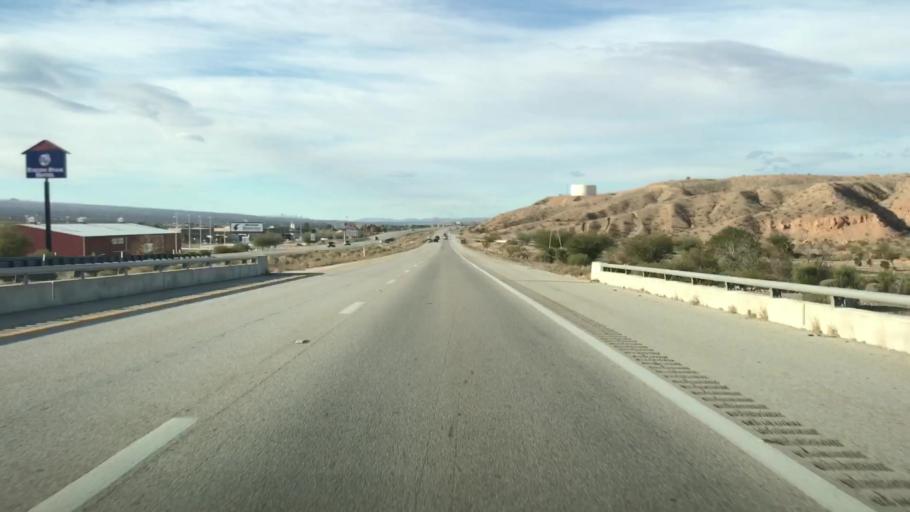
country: US
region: Nevada
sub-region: Clark County
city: Mesquite
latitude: 36.8127
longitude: -114.0647
